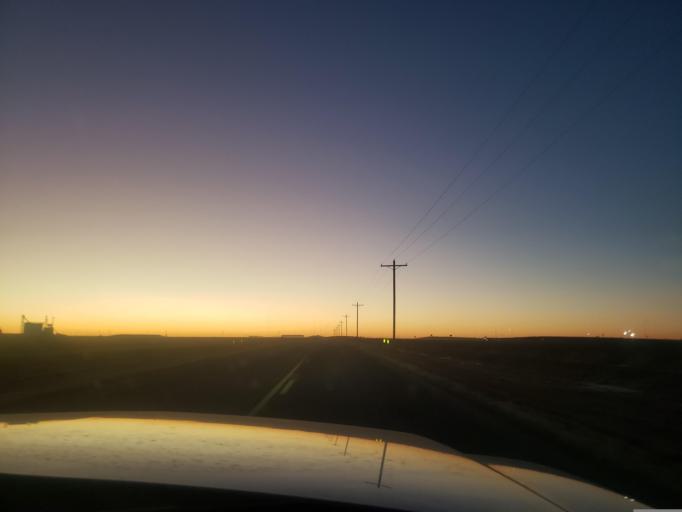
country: US
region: Kansas
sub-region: Finney County
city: Garden City
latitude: 38.0007
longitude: -100.8754
